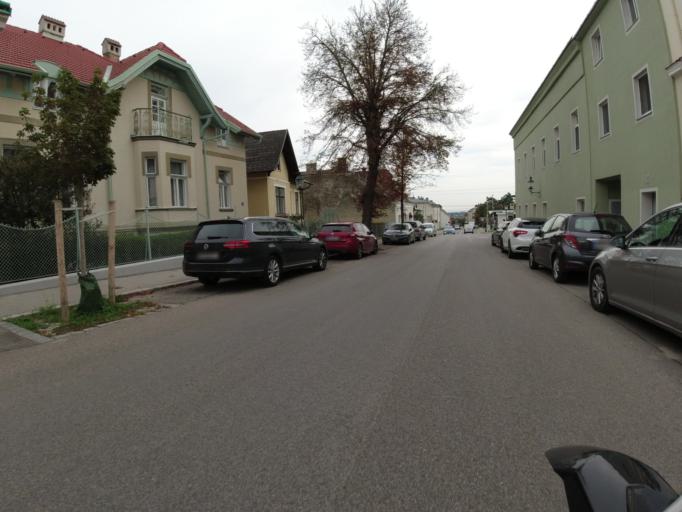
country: AT
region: Lower Austria
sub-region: Politischer Bezirk Modling
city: Gumpoldskirchen
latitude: 48.0420
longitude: 16.2848
